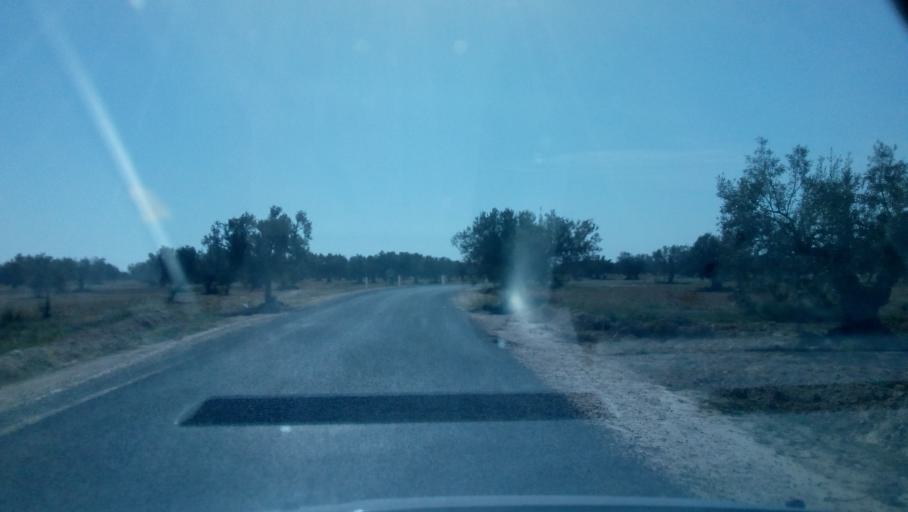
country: TN
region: Safaqis
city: Jabinyanah
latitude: 34.8765
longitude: 10.8836
